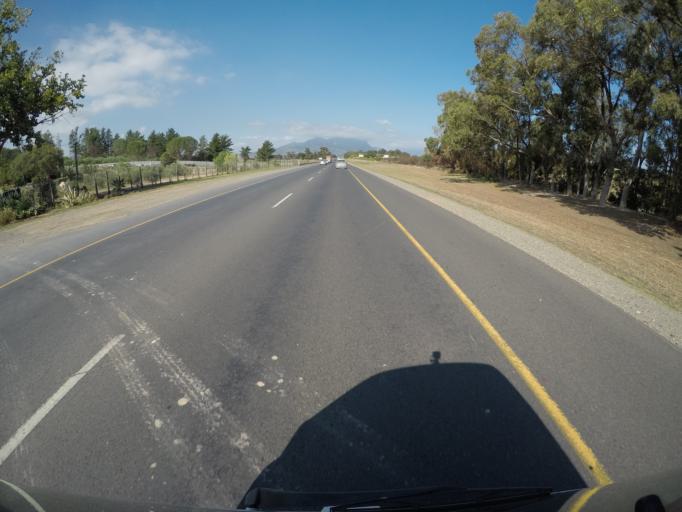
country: ZA
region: Western Cape
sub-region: City of Cape Town
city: Kraaifontein
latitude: -33.8779
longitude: 18.7787
